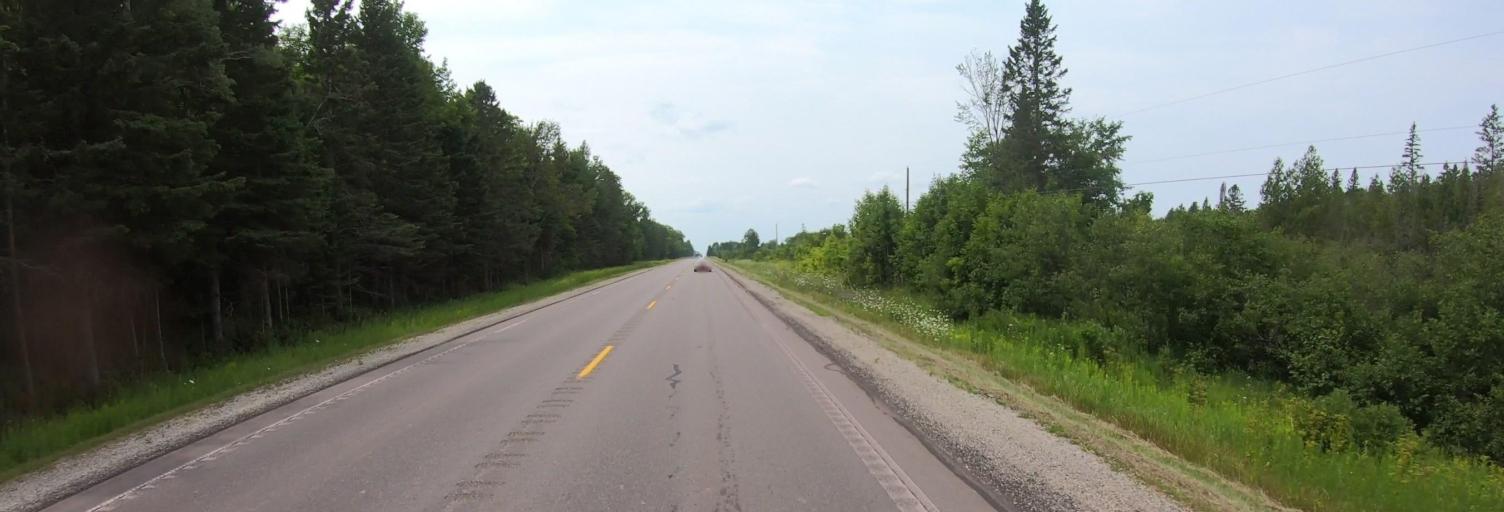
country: US
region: Michigan
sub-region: Marquette County
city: K. I. Sawyer Air Force Base
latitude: 46.3478
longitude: -87.1396
